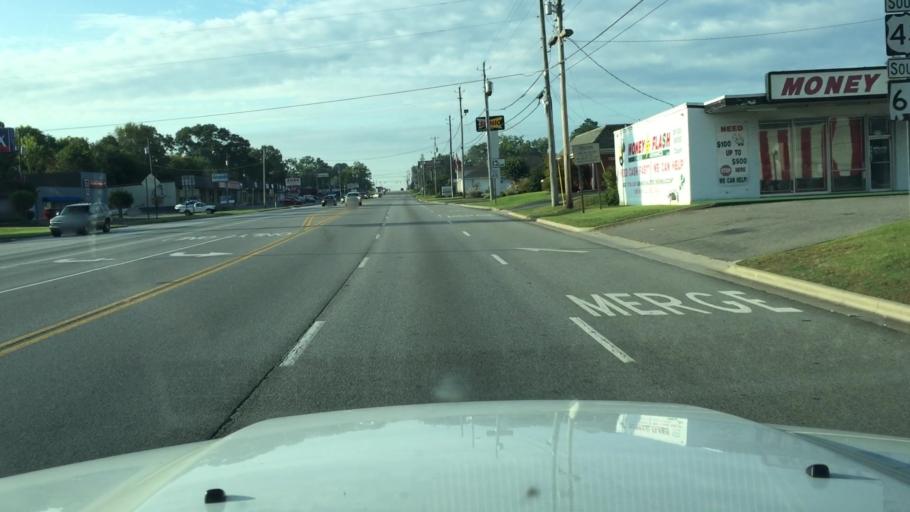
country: US
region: Alabama
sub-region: Tuscaloosa County
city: Northport
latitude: 33.2381
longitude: -87.5767
